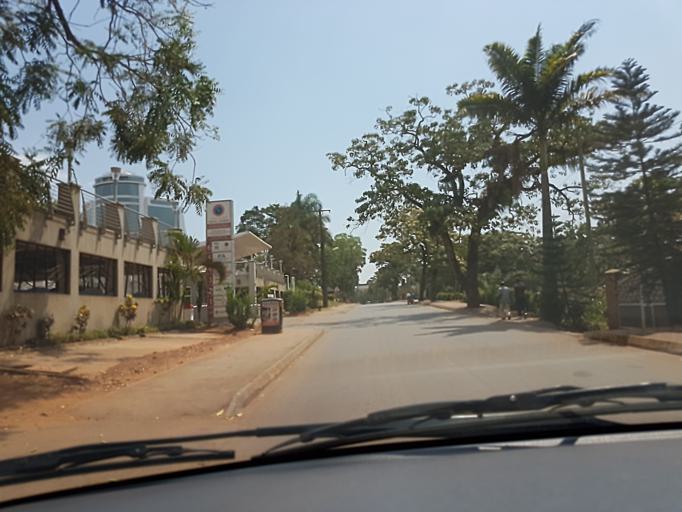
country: UG
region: Central Region
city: Kampala Central Division
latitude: 0.3268
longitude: 32.5769
